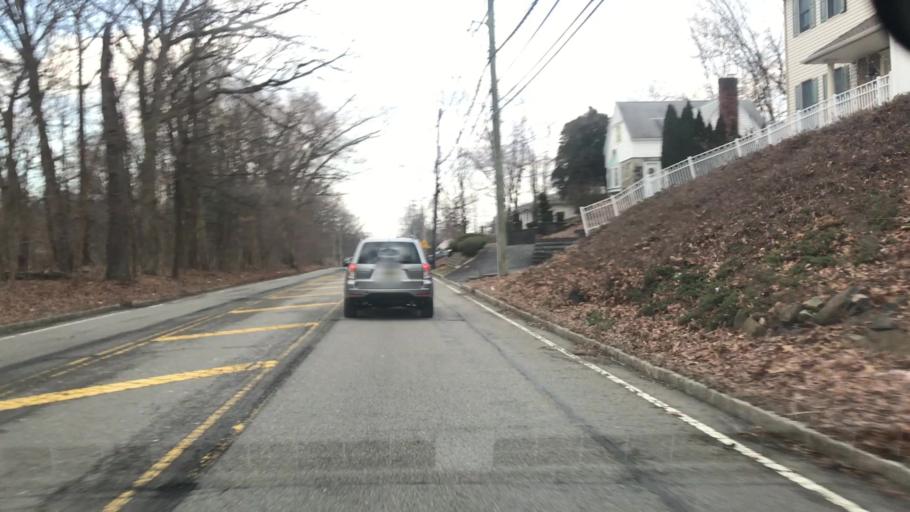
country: US
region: New Jersey
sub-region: Essex County
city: Roseland
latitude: 40.8049
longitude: -74.2909
